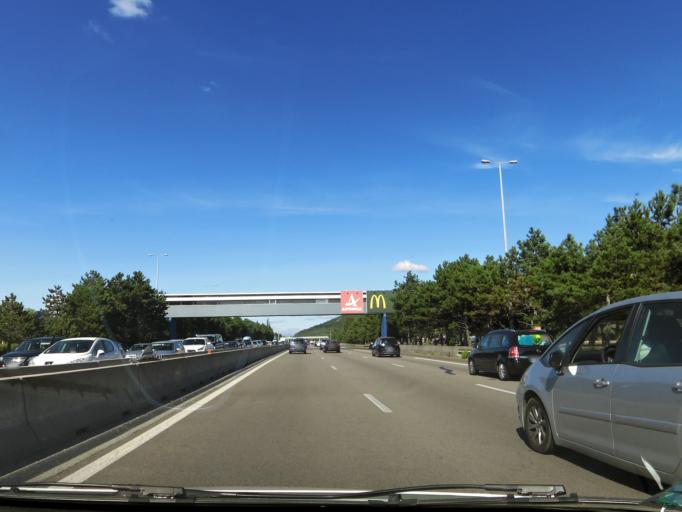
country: FR
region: Rhone-Alpes
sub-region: Departement de la Drome
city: Allan
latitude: 44.5150
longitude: 4.7815
